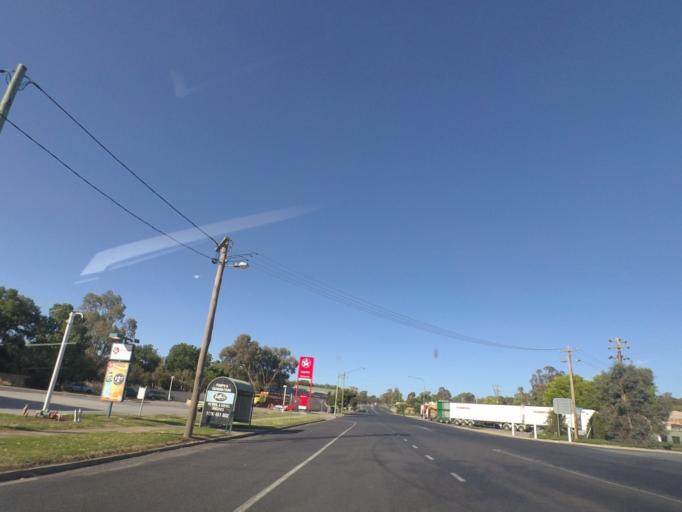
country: AU
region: New South Wales
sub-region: Wagga Wagga
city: Forest Hill
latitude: -35.2776
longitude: 147.7359
